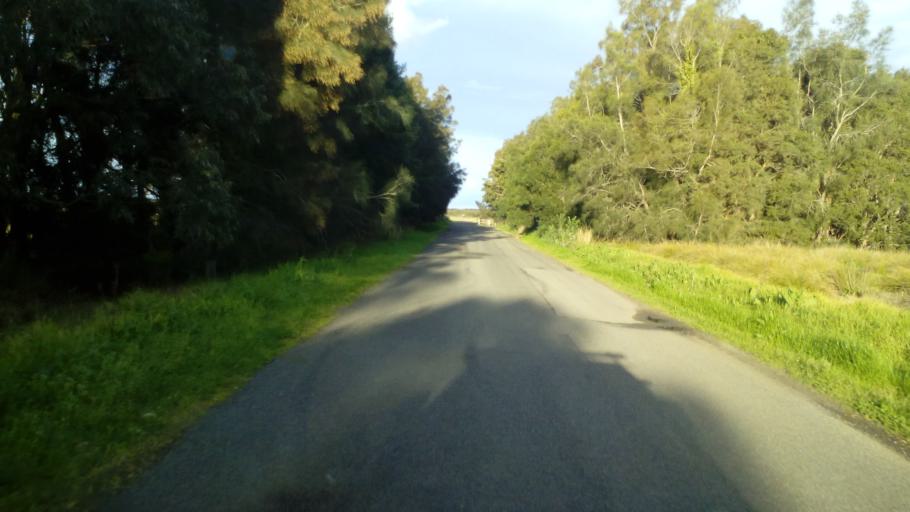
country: AU
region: New South Wales
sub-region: Newcastle
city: Mayfield West
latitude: -32.8412
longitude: 151.7134
